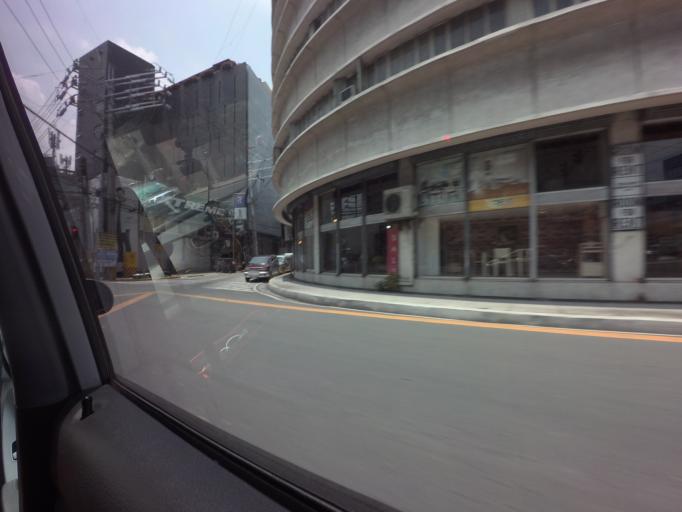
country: PH
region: Metro Manila
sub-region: City of Manila
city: Quiapo
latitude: 14.5926
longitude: 120.9873
